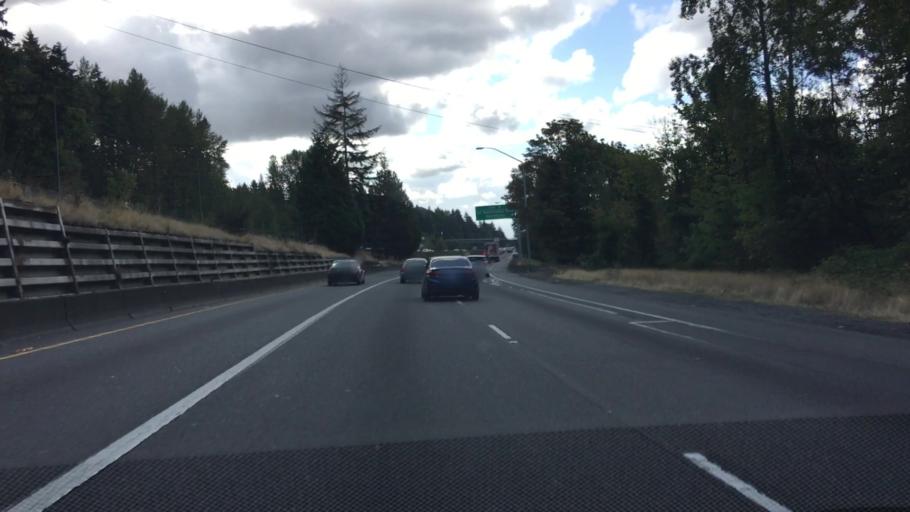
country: US
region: Washington
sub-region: King County
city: Newport
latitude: 47.5609
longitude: -122.1876
